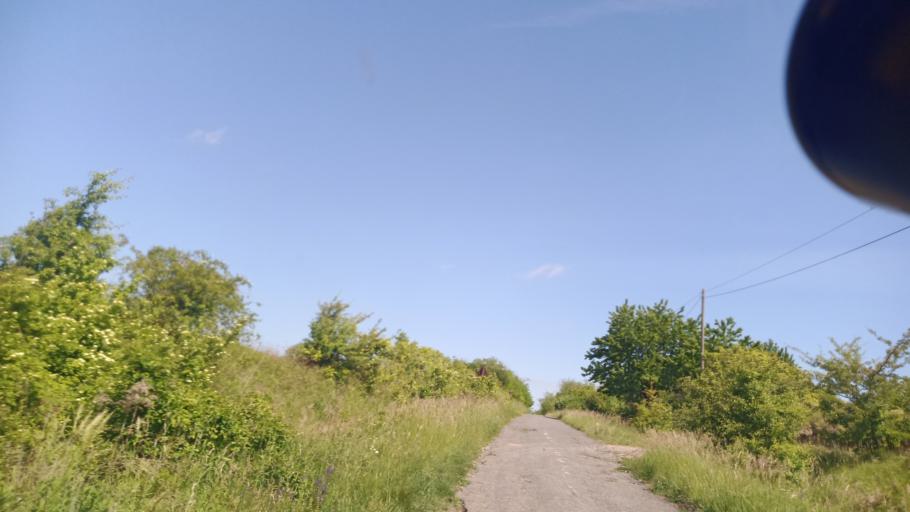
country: HU
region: Zala
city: Pacsa
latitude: 46.6569
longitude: 17.0632
